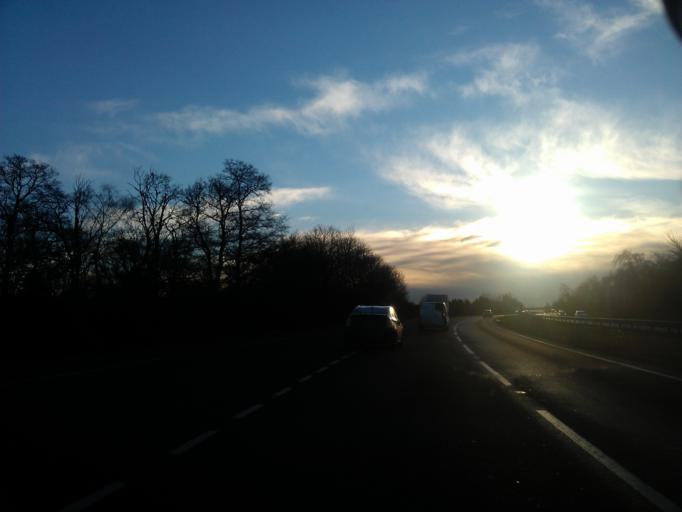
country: GB
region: England
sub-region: Essex
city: Colchester
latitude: 51.9201
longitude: 0.9400
